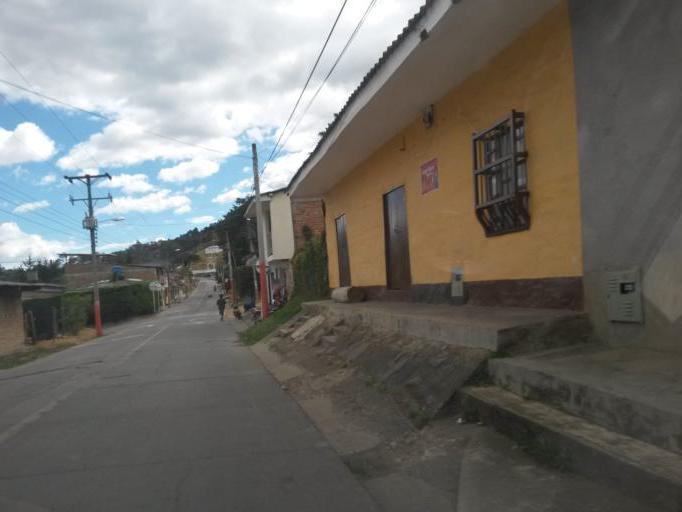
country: CO
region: Cauca
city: Silvia
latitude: 2.6092
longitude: -76.3849
